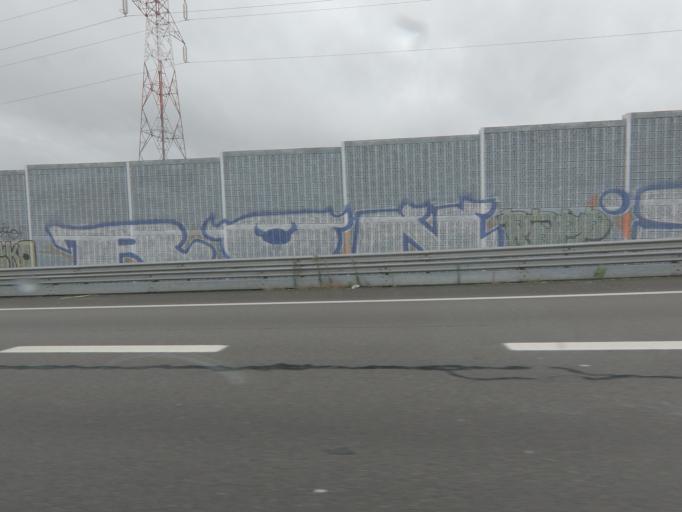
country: PT
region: Porto
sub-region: Maia
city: Leca do Bailio
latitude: 41.2048
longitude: -8.6230
